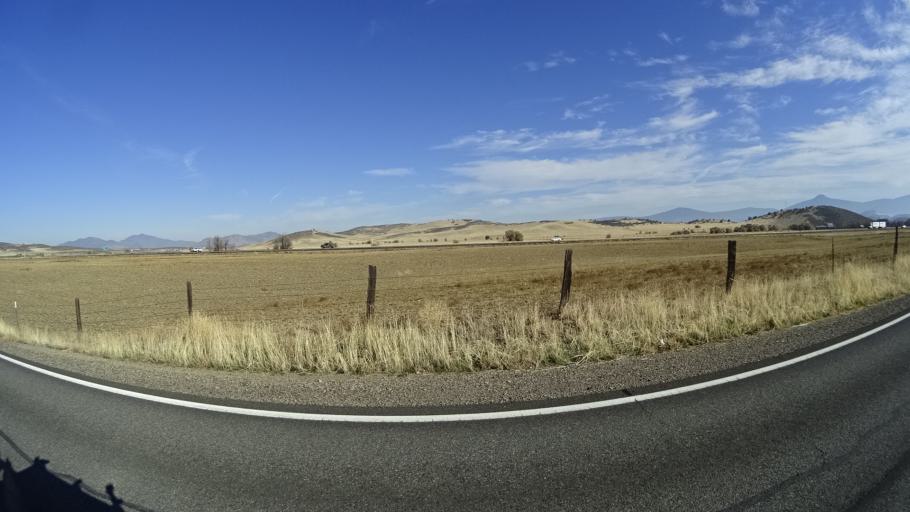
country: US
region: California
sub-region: Siskiyou County
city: Montague
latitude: 41.6493
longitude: -122.5493
